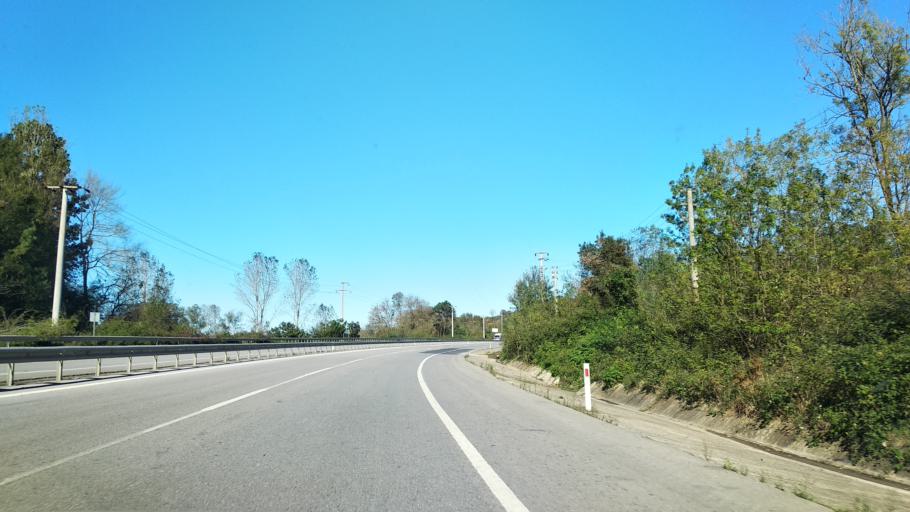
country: TR
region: Sakarya
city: Karasu
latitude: 41.0894
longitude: 30.6478
